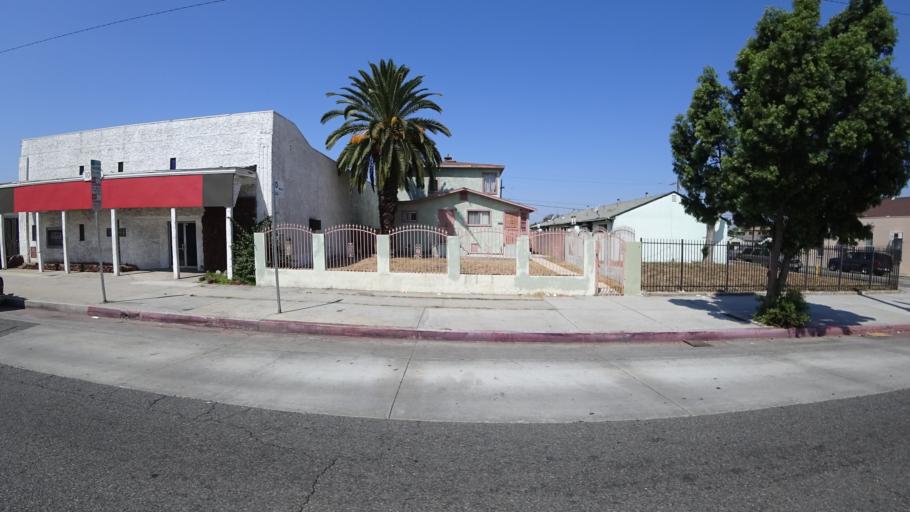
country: US
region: California
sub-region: Los Angeles County
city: Westmont
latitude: 33.9411
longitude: -118.2919
